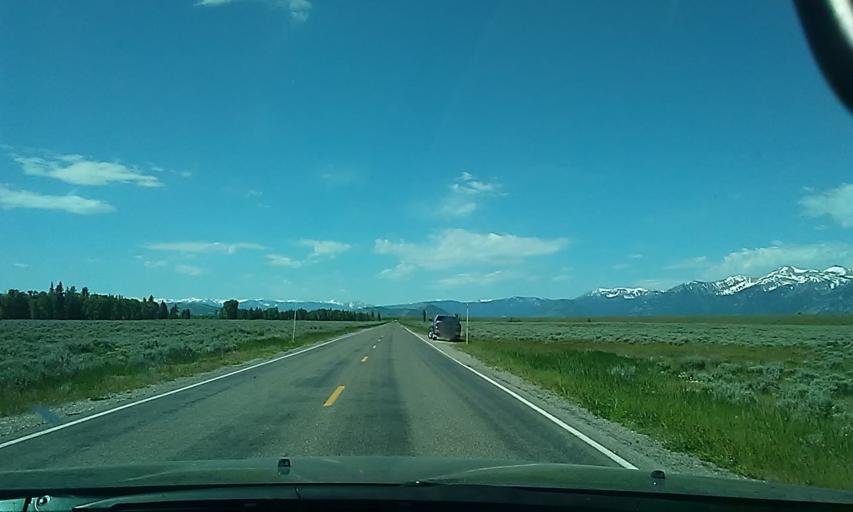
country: US
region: Wyoming
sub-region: Teton County
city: Jackson
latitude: 43.6150
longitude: -110.6780
